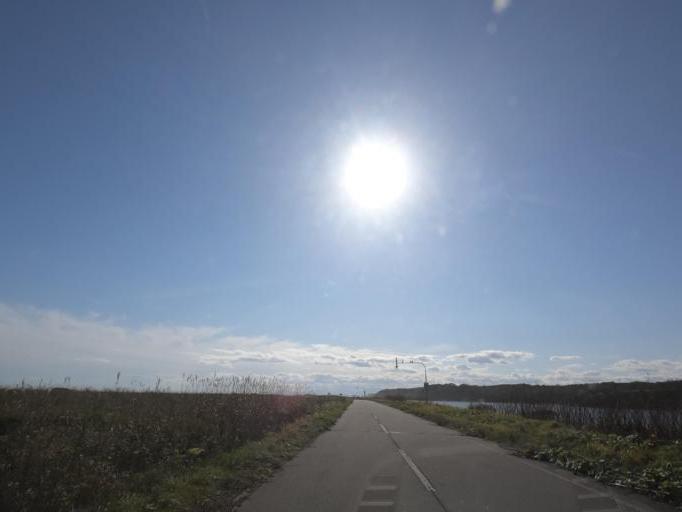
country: JP
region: Hokkaido
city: Obihiro
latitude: 42.5822
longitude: 143.5315
